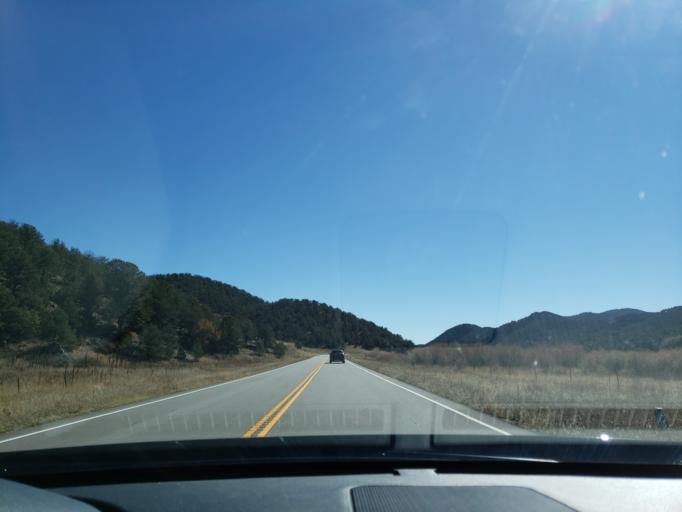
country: US
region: Colorado
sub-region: Fremont County
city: Canon City
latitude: 38.6352
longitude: -105.4649
